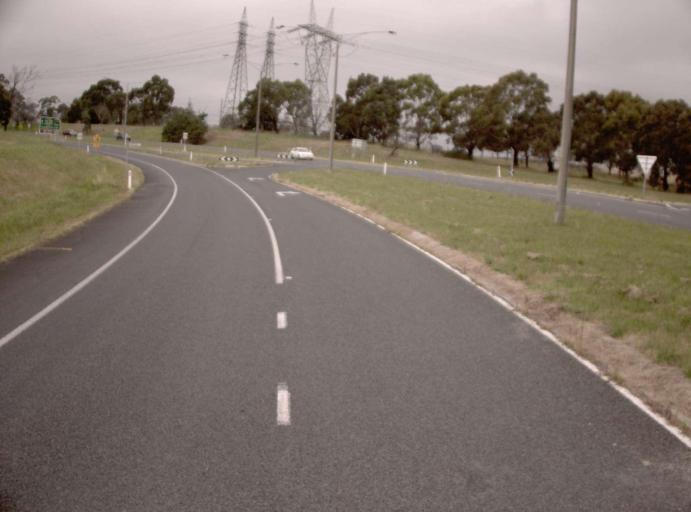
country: AU
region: Victoria
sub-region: Latrobe
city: Traralgon
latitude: -38.2481
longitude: 146.5480
